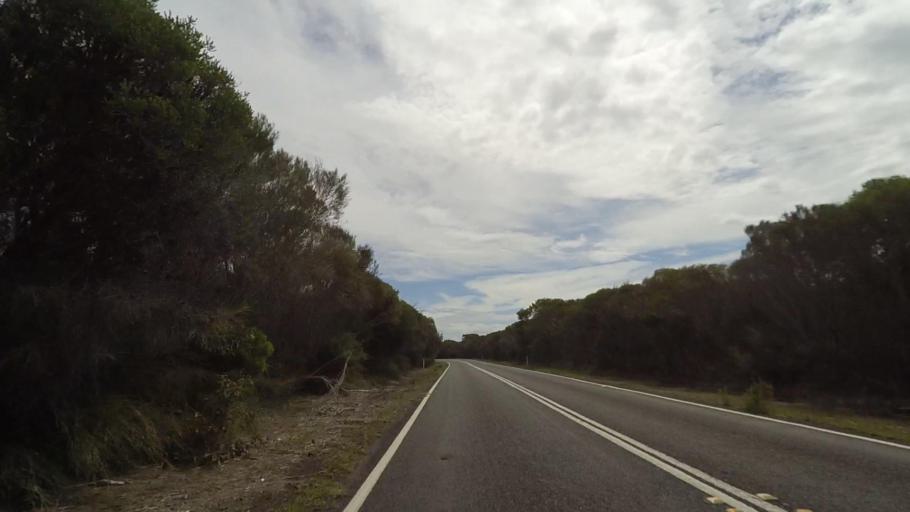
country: AU
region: New South Wales
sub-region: Sutherland Shire
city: Bundeena
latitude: -34.0956
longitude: 151.1273
